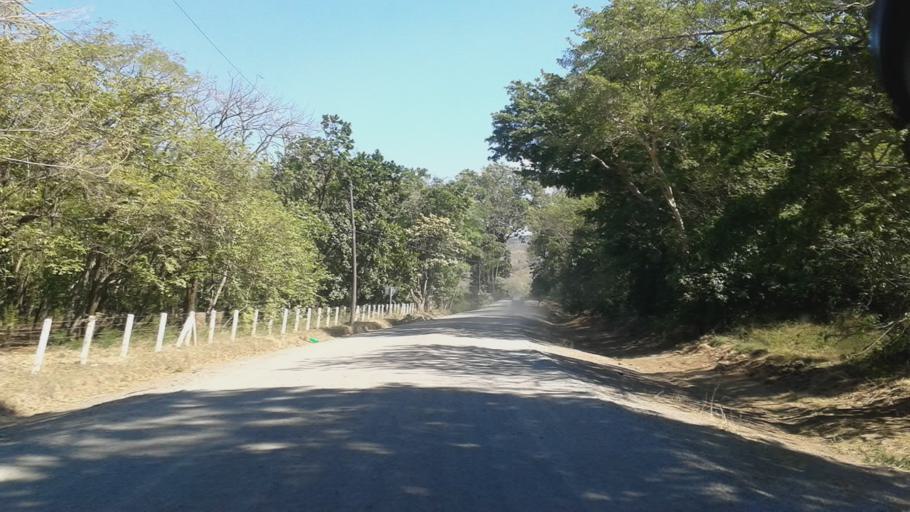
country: CR
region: Guanacaste
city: Santa Cruz
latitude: 10.1985
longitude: -85.7622
